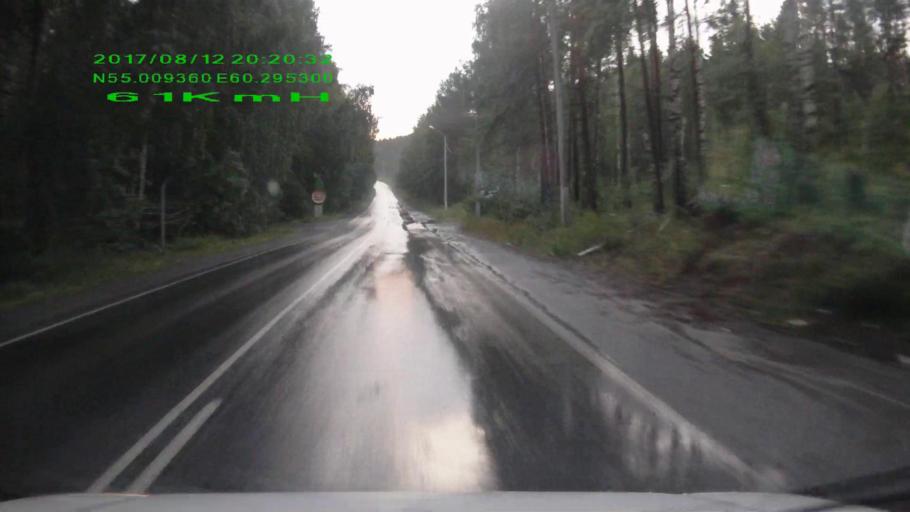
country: RU
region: Chelyabinsk
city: Chebarkul'
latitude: 55.0095
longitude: 60.2947
